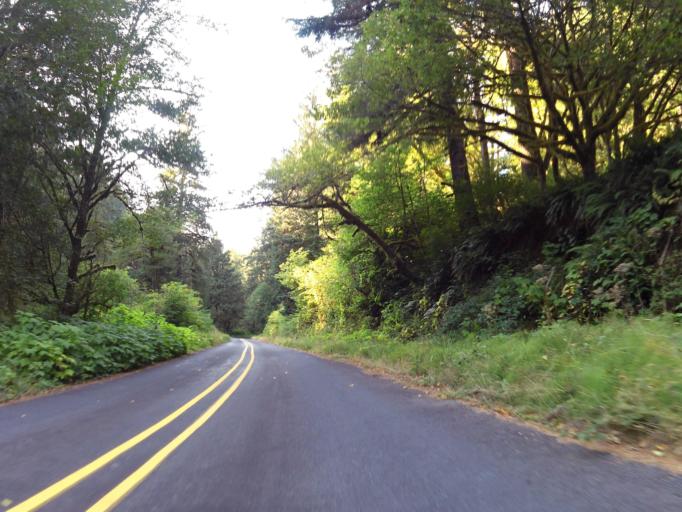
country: US
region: Oregon
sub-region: Lincoln County
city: Rose Lodge
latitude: 45.0357
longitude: -123.9114
